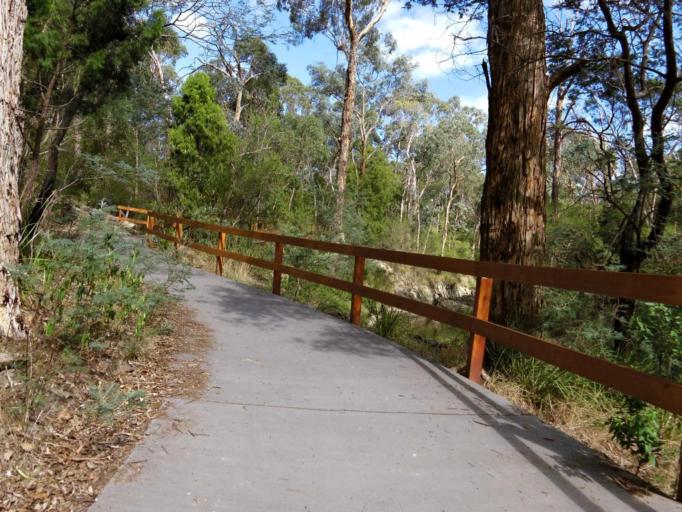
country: AU
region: Victoria
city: Mitcham
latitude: -37.7968
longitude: 145.2040
